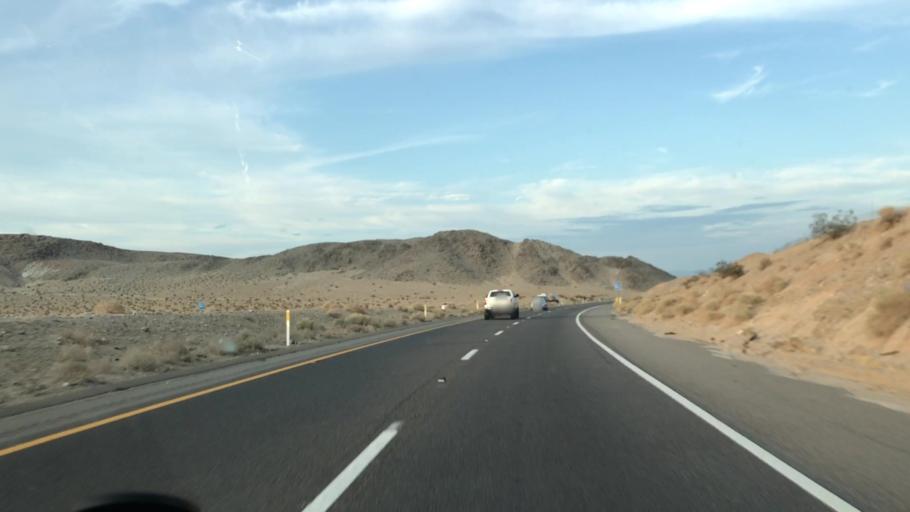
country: US
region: California
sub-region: San Bernardino County
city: Fort Irwin
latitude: 35.0784
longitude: -116.4002
